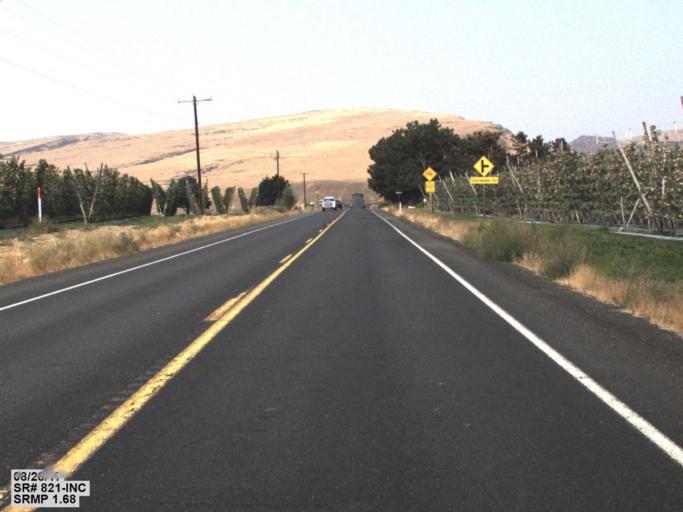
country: US
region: Washington
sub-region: Yakima County
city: Selah
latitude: 46.6996
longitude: -120.4745
